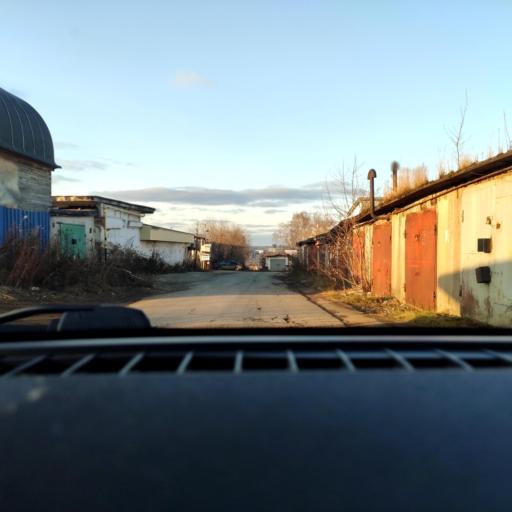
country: RU
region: Perm
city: Perm
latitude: 57.9839
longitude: 56.2376
